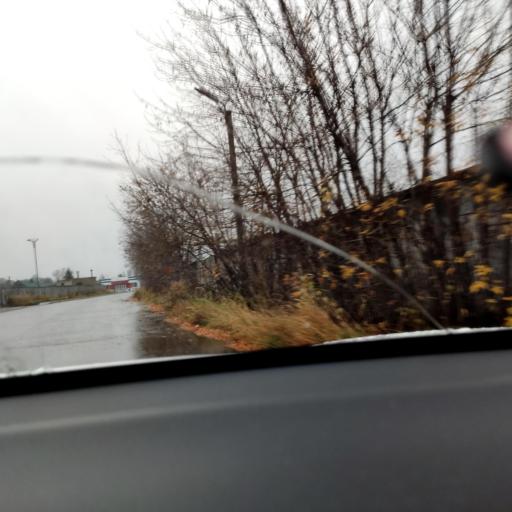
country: RU
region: Tatarstan
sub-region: Gorod Kazan'
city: Kazan
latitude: 55.8663
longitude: 49.1093
